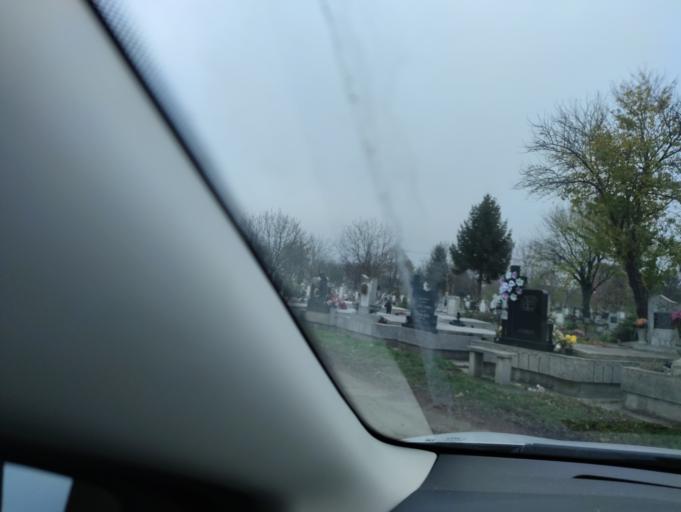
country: RO
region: Bihor
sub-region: Comuna Biharea
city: Oradea
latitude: 47.0374
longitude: 21.9241
